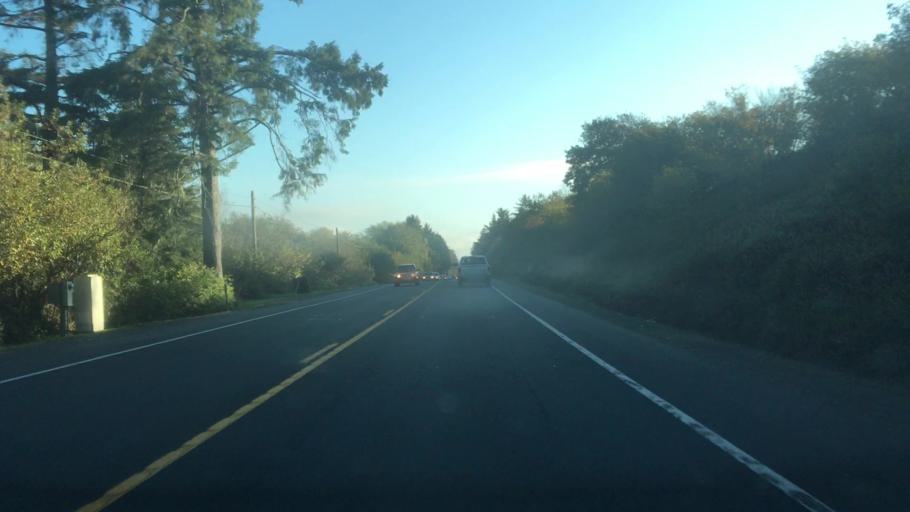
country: US
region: Oregon
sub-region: Clatsop County
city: Gearhart
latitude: 46.0664
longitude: -123.9162
